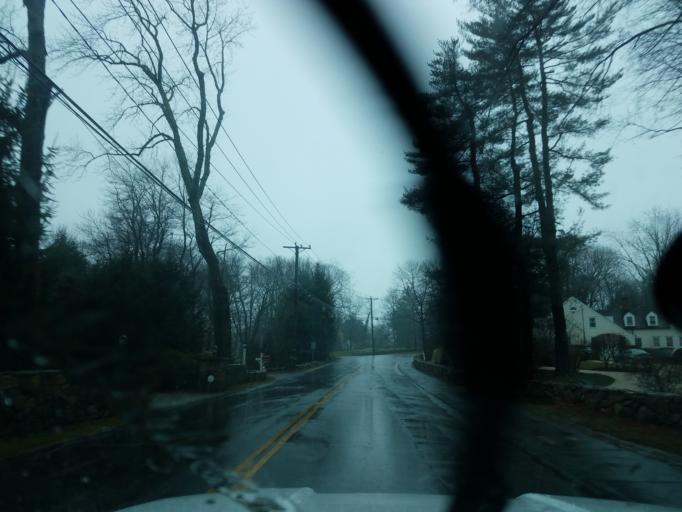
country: US
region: Connecticut
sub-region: Fairfield County
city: Darien
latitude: 41.0840
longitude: -73.4799
